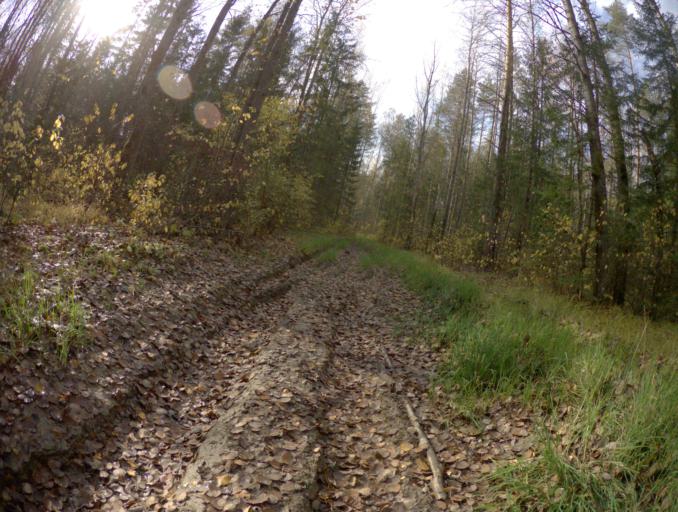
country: RU
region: Vladimir
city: Raduzhnyy
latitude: 55.9586
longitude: 40.3501
